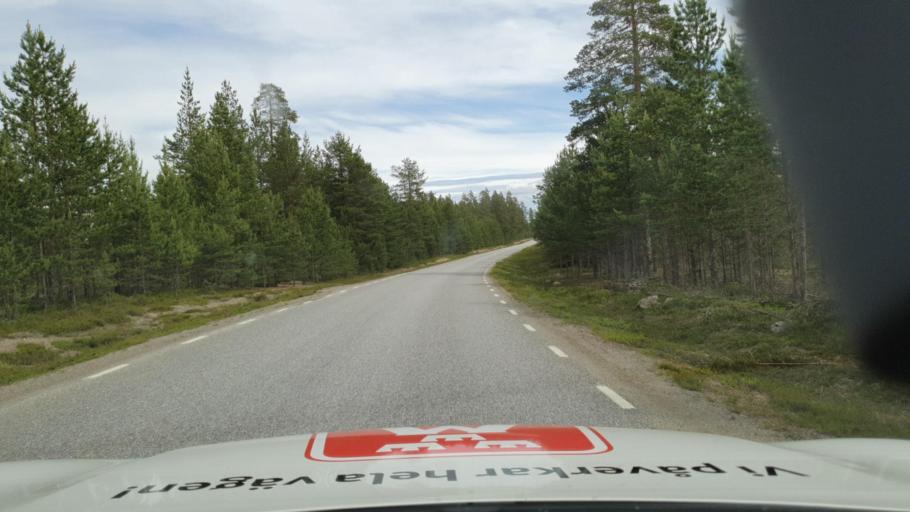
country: SE
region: Vaesterbotten
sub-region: Skelleftea Kommun
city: Burtraesk
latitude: 64.5055
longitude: 20.7988
